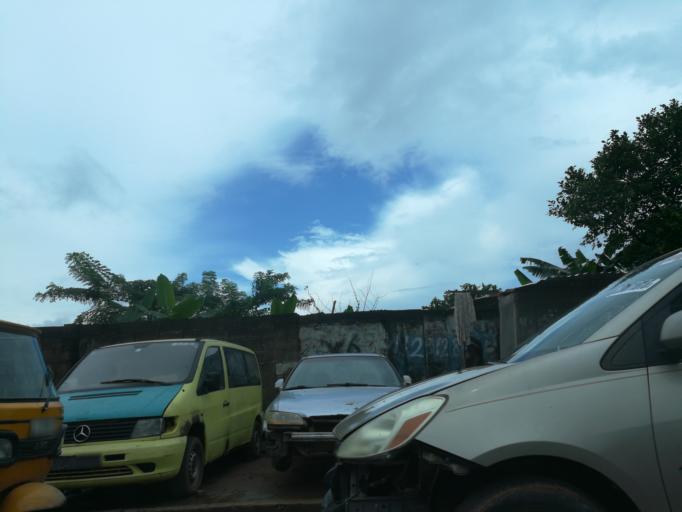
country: NG
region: Lagos
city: Agege
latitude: 6.6137
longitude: 3.3214
